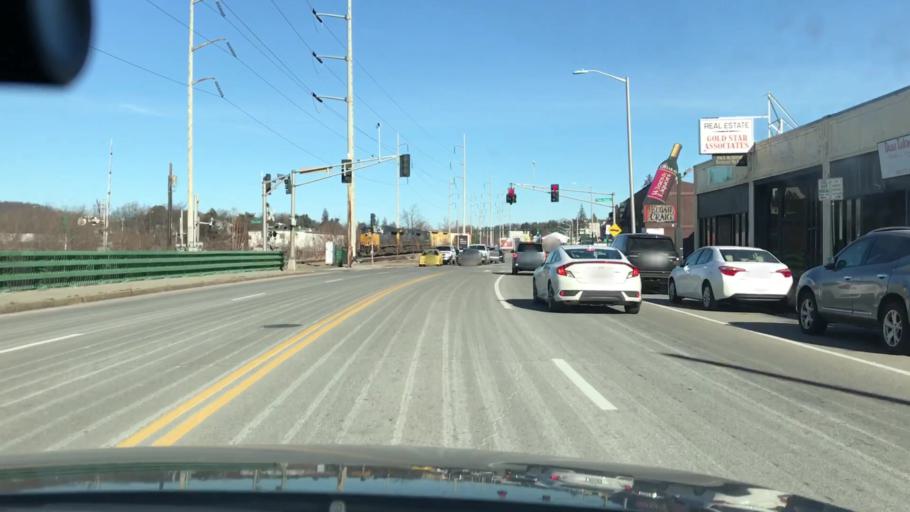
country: US
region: Massachusetts
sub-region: Worcester County
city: Worcester
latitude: 42.3046
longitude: -71.8008
